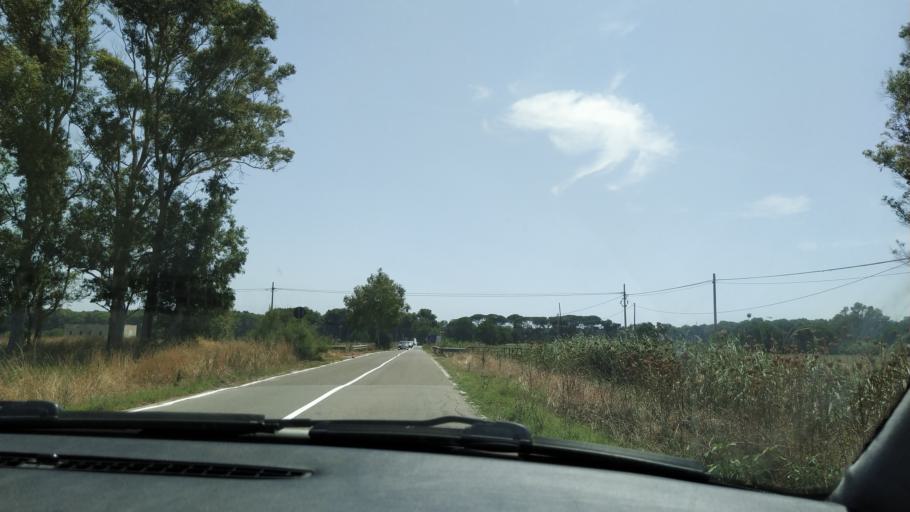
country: IT
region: Basilicate
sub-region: Provincia di Matera
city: Marconia
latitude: 40.3258
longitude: 16.7905
